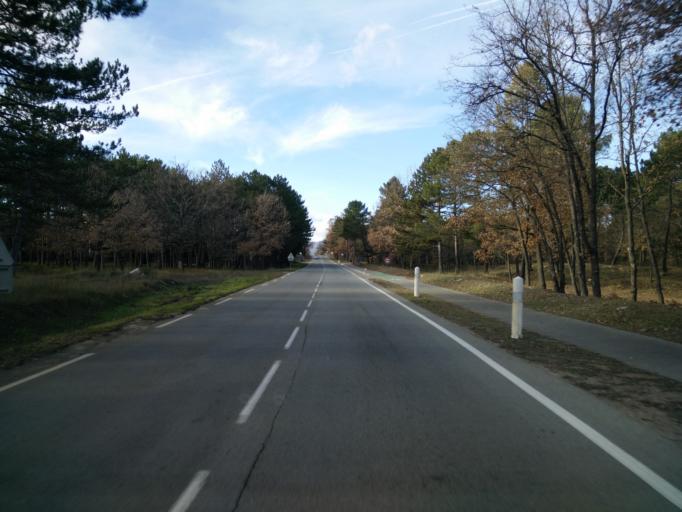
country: FR
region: Provence-Alpes-Cote d'Azur
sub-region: Departement des Alpes-Maritimes
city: Le Tignet
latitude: 43.6477
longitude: 6.8234
